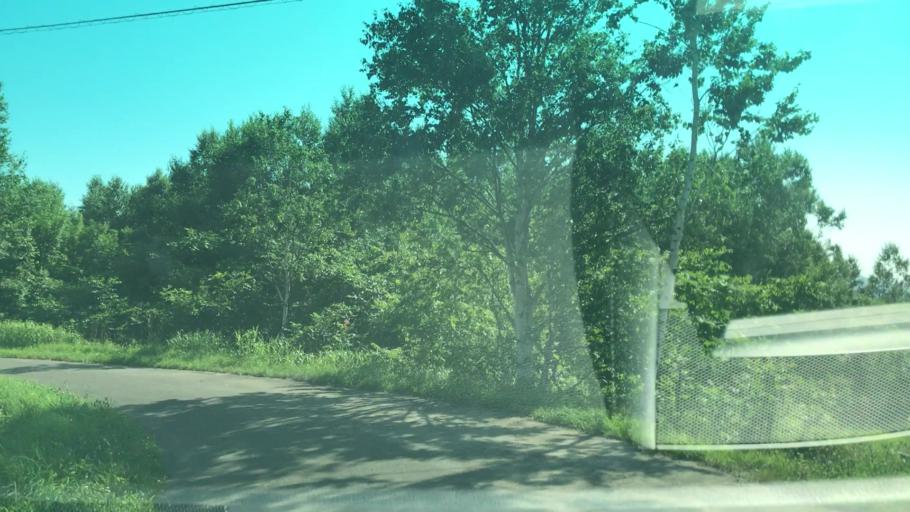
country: JP
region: Hokkaido
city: Iwanai
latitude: 42.9726
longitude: 140.6098
